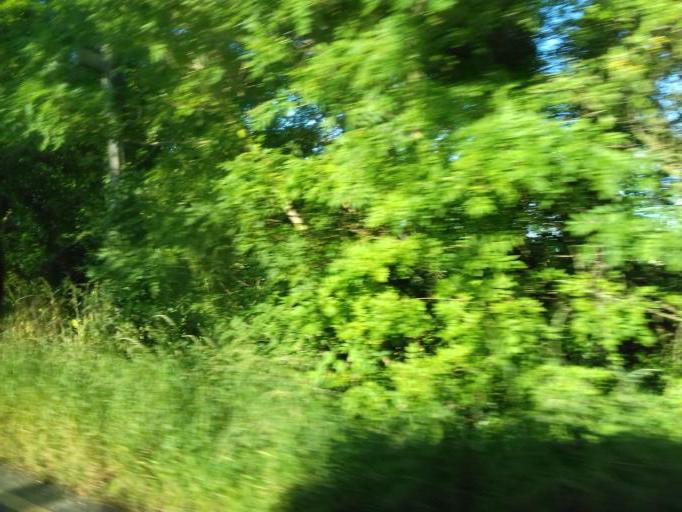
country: IE
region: Leinster
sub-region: An Mhi
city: Ashbourne
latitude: 53.4824
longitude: -6.3300
